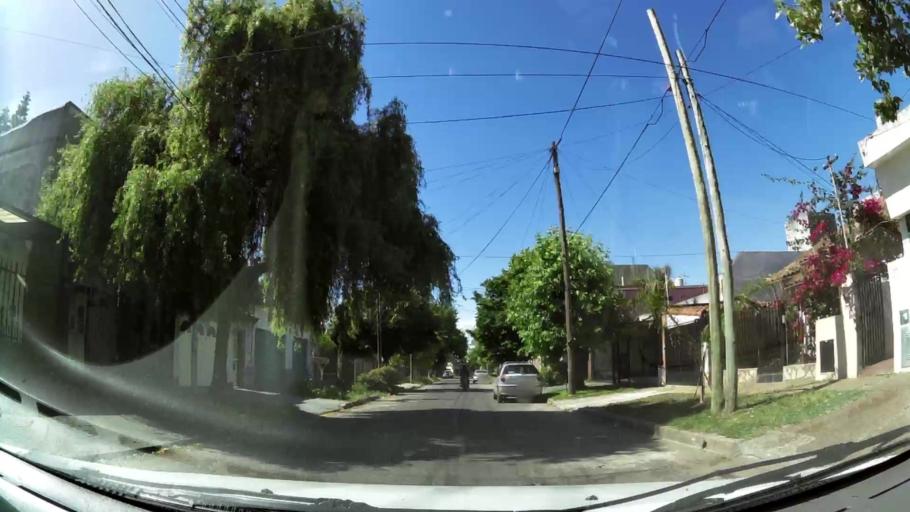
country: AR
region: Buenos Aires
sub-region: Partido de General San Martin
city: General San Martin
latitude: -34.5400
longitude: -58.5753
